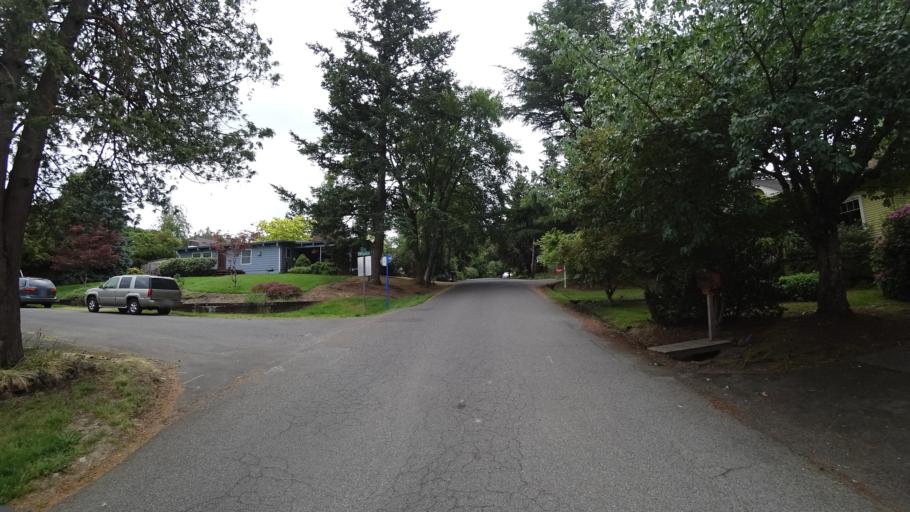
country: US
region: Oregon
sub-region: Washington County
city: Garden Home-Whitford
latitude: 45.4742
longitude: -122.7335
